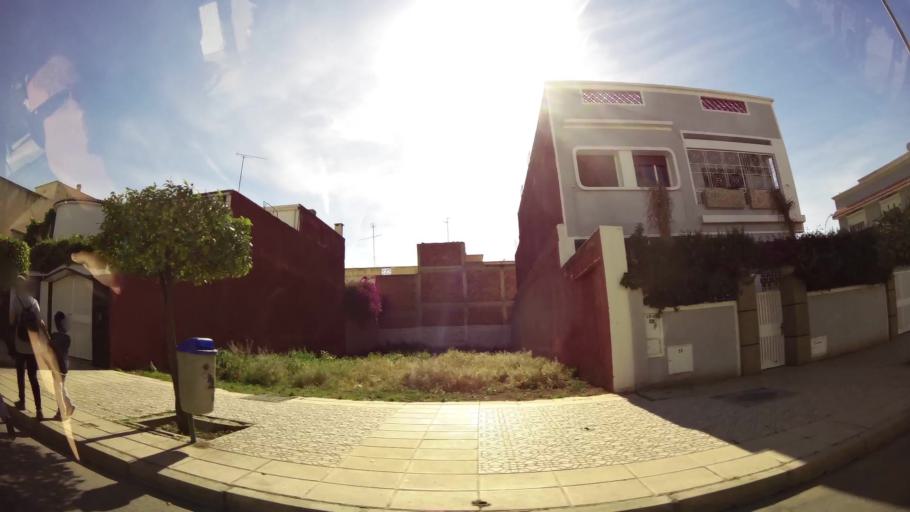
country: MA
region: Oriental
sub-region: Oujda-Angad
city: Oujda
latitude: 34.6694
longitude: -1.9065
